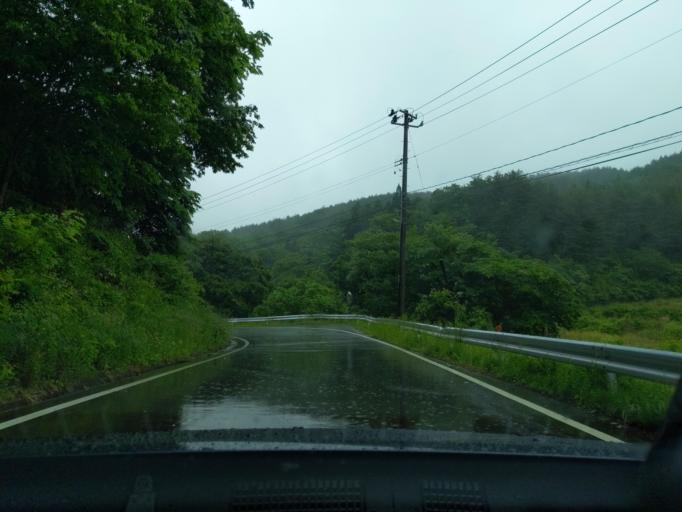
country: JP
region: Fukushima
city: Funehikimachi-funehiki
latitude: 37.6403
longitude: 140.7288
